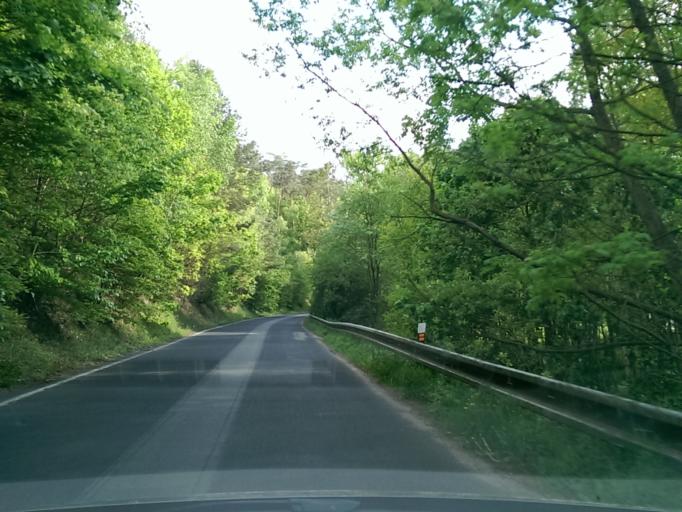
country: CZ
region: Central Bohemia
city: Bakov nad Jizerou
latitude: 50.4960
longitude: 14.8918
